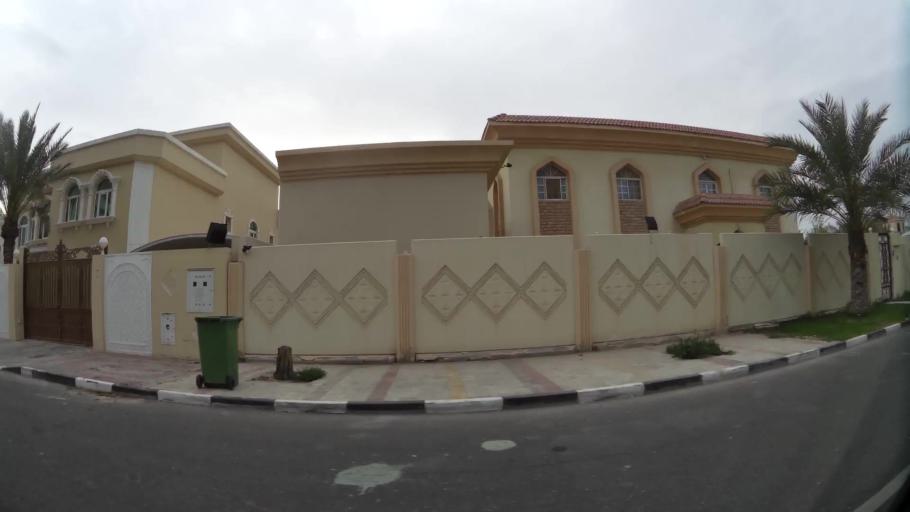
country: QA
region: Baladiyat ad Dawhah
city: Doha
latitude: 25.3257
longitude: 51.5105
